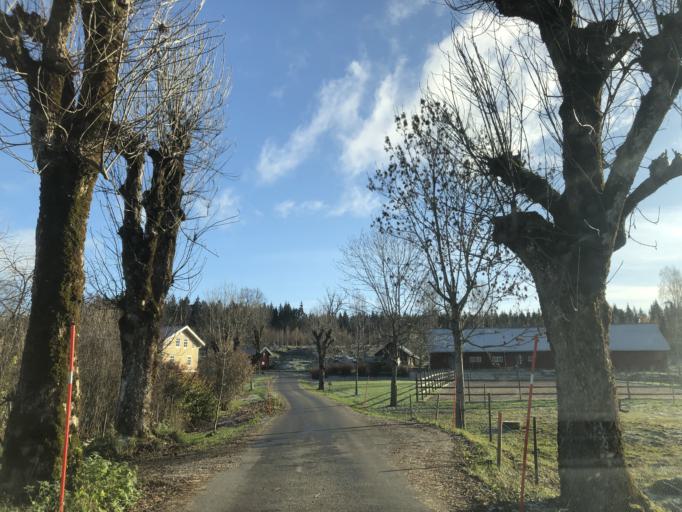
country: SE
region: Vaestra Goetaland
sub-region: Ulricehamns Kommun
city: Ulricehamn
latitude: 57.7253
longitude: 13.4106
